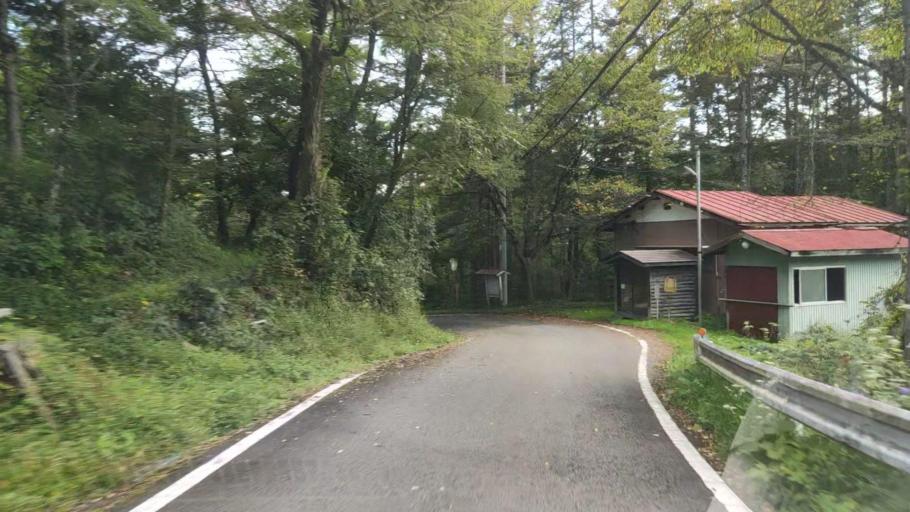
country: JP
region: Gunma
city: Nakanojomachi
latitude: 36.6570
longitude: 138.6305
